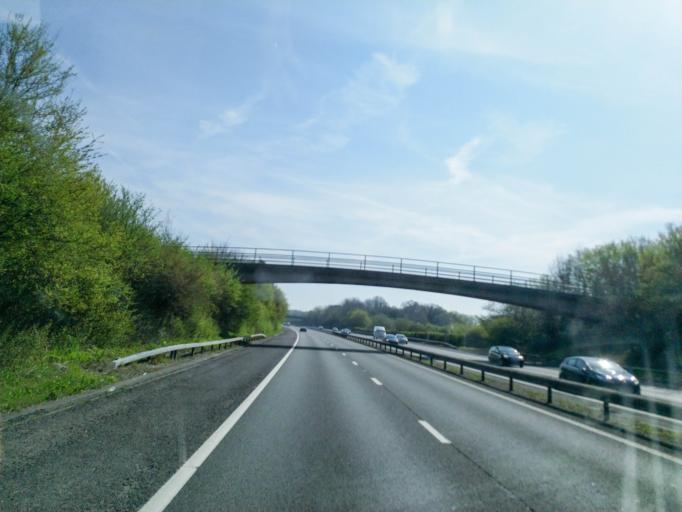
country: GB
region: England
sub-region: Kent
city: Kemsing
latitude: 51.3009
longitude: 0.2240
